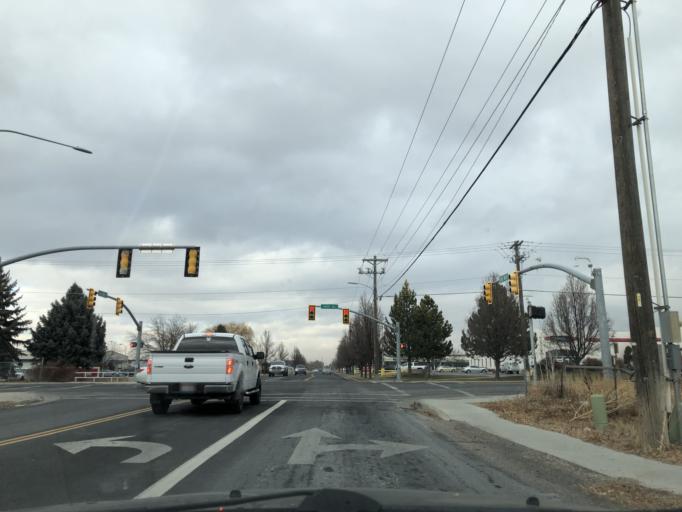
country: US
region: Utah
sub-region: Cache County
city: Logan
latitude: 41.7574
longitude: -111.8392
